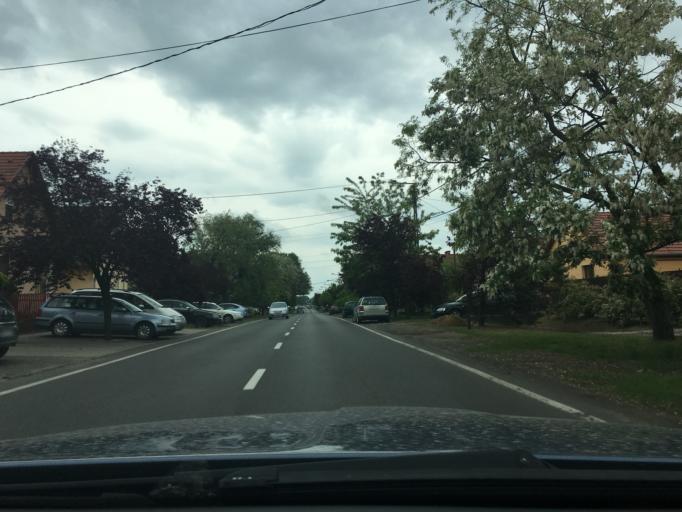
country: HU
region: Hajdu-Bihar
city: Debrecen
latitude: 47.5455
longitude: 21.6714
